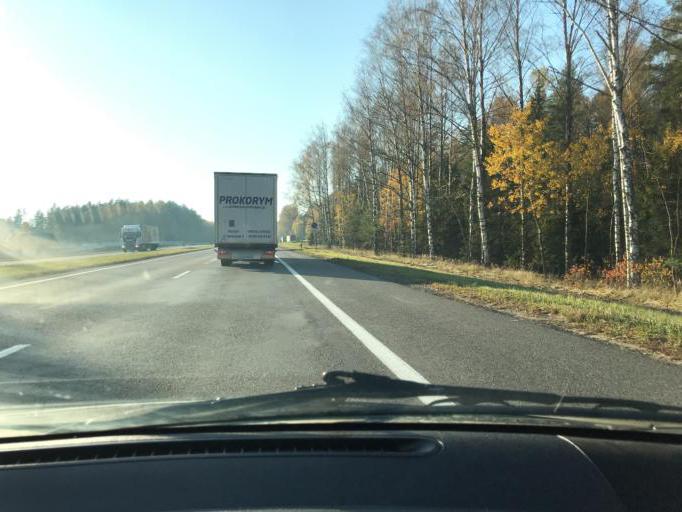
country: BY
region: Minsk
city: Krupki
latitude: 54.3008
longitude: 28.9537
